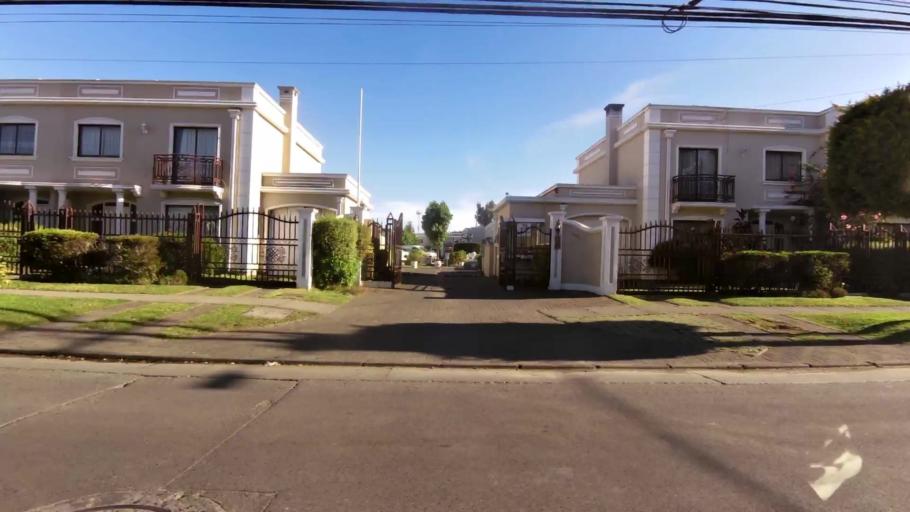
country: CL
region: Biobio
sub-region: Provincia de Concepcion
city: Concepcion
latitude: -36.8347
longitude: -73.1048
